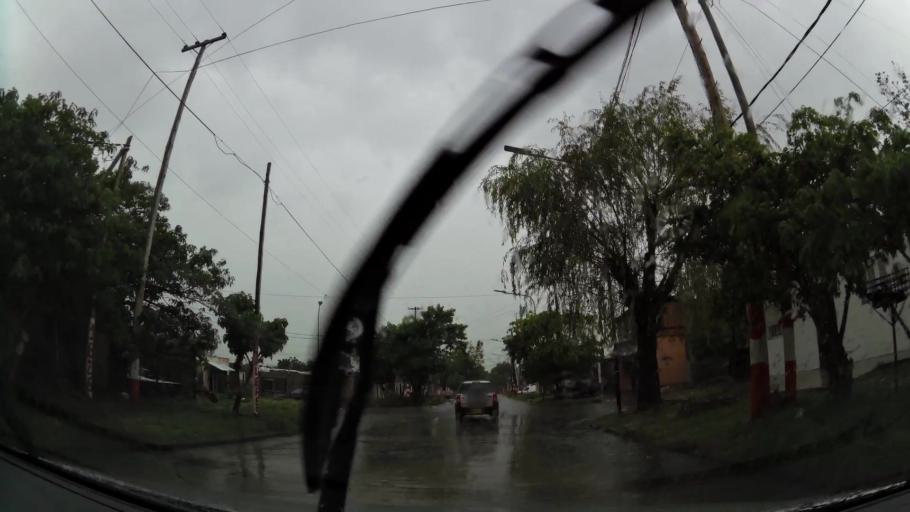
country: AR
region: Buenos Aires
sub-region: Partido de Lanus
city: Lanus
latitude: -34.7201
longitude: -58.4043
